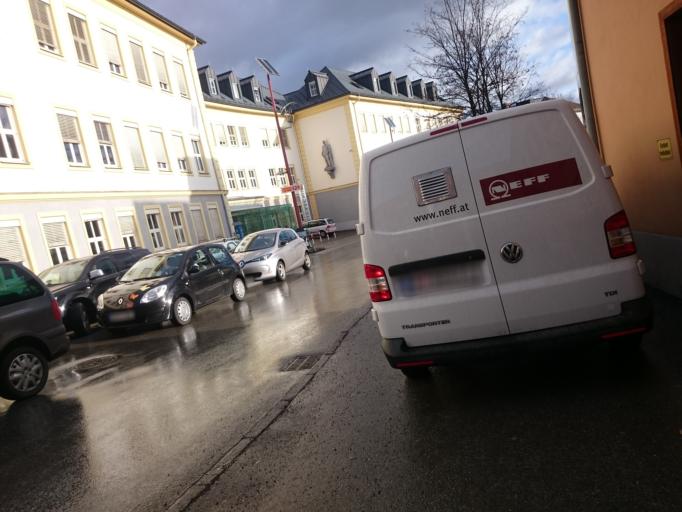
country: AT
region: Styria
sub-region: Politischer Bezirk Weiz
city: Weiz
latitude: 47.2184
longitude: 15.6222
